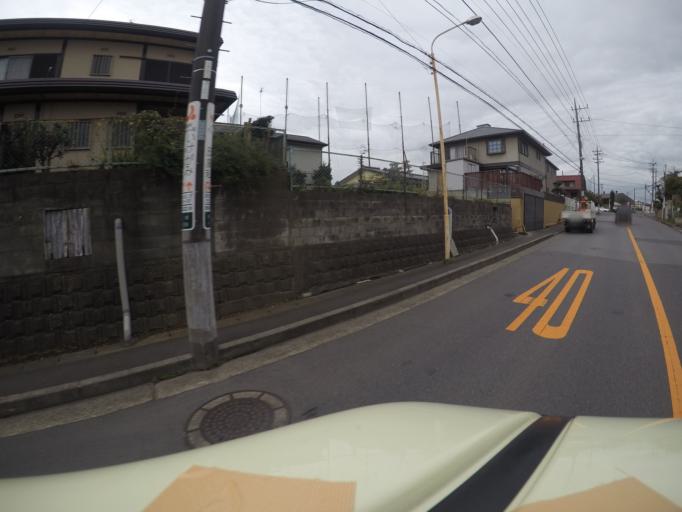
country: JP
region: Ibaraki
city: Naka
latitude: 36.0680
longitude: 140.1720
